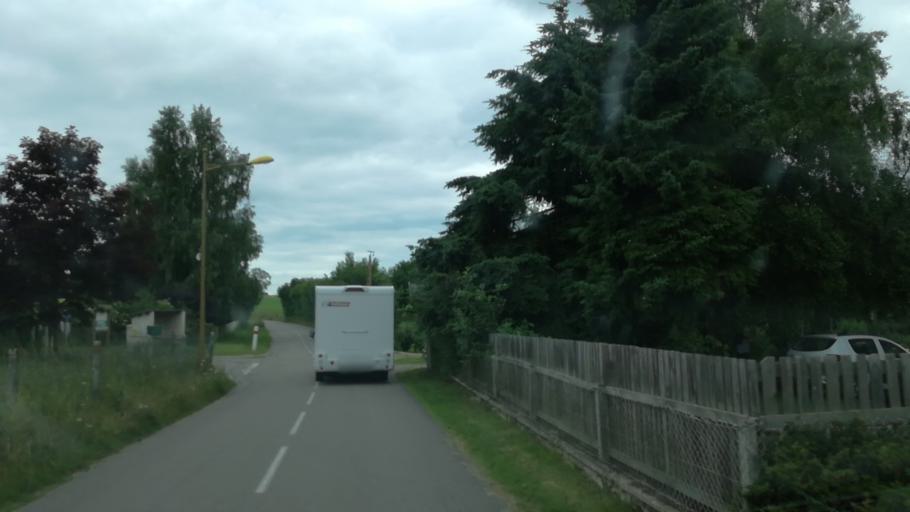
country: FR
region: Haute-Normandie
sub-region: Departement de l'Eure
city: Bourg-Achard
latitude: 49.3323
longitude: 0.8116
